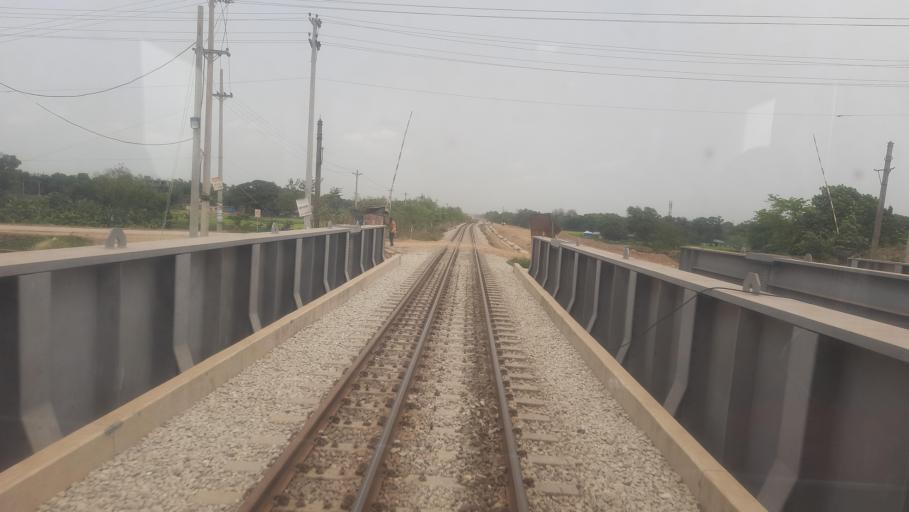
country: BD
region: Chittagong
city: Comilla
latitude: 23.4867
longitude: 91.1624
